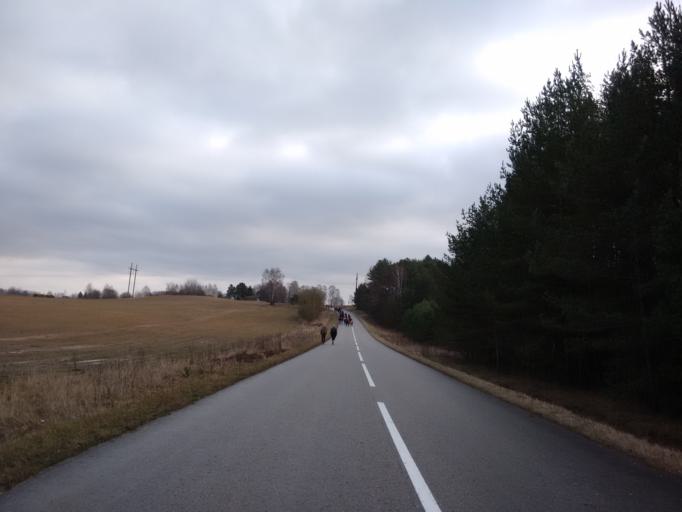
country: LT
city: Veisiejai
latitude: 54.2437
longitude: 23.8532
